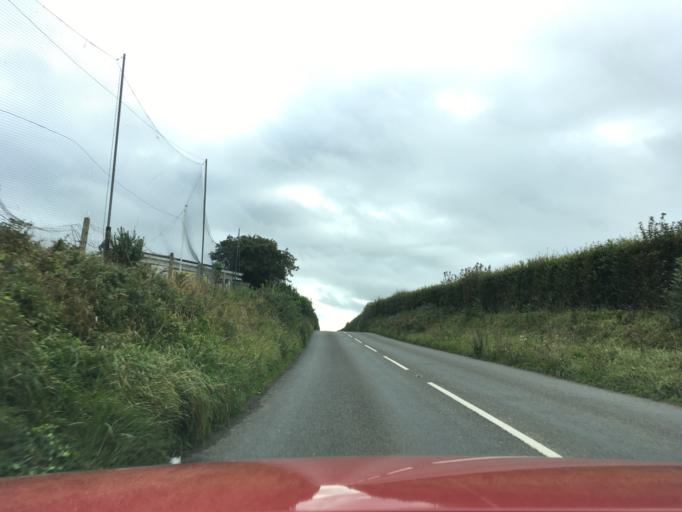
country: GB
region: England
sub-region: Devon
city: Kingsbridge
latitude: 50.2801
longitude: -3.7987
